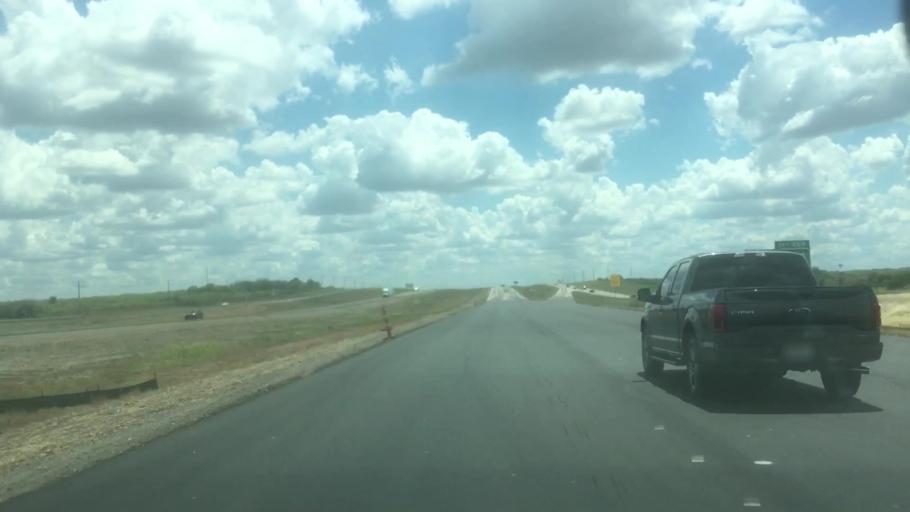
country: US
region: Texas
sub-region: Caldwell County
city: Lockhart
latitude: 29.9878
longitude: -97.6834
